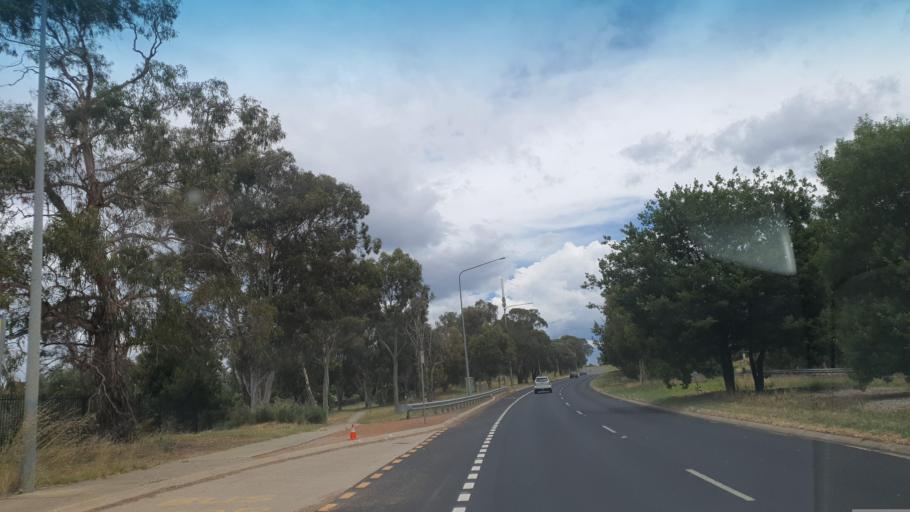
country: AU
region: Australian Capital Territory
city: Macquarie
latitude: -35.2234
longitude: 149.0391
